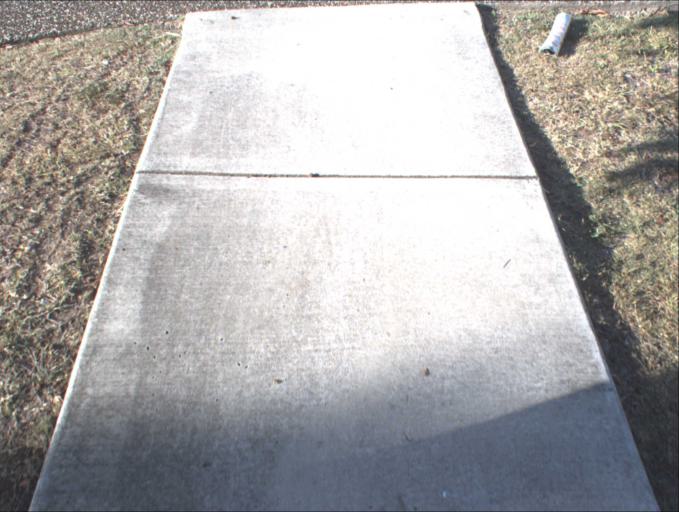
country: AU
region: Queensland
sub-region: Logan
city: Beenleigh
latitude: -27.6876
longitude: 153.1782
